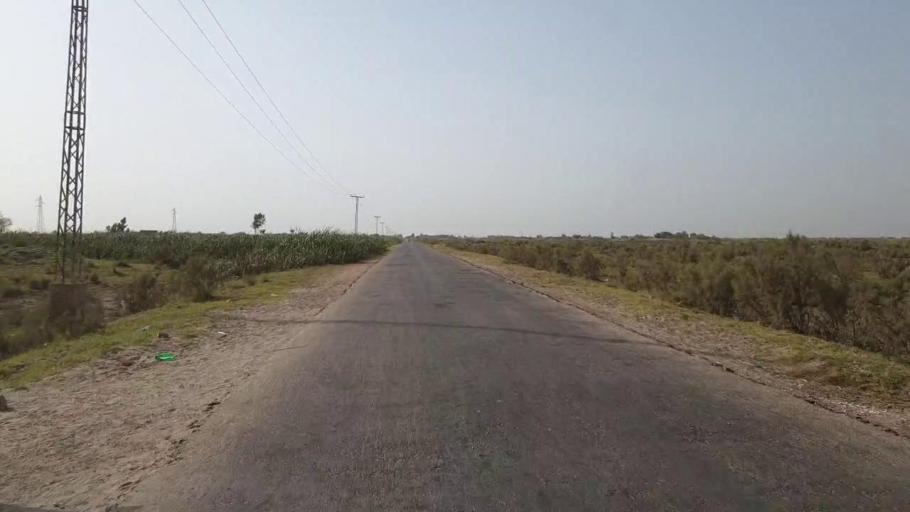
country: PK
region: Sindh
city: Khadro
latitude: 26.3483
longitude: 68.9236
